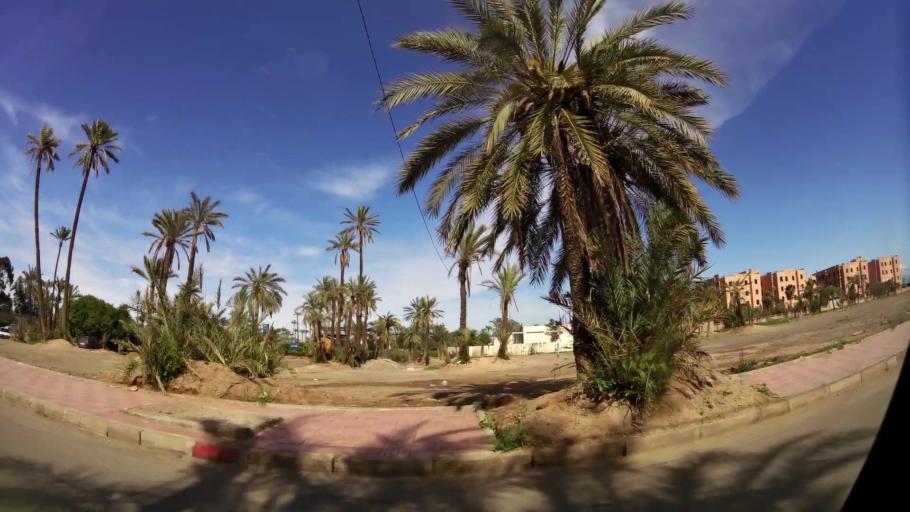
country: MA
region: Marrakech-Tensift-Al Haouz
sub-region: Marrakech
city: Marrakesh
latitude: 31.6452
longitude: -7.9782
